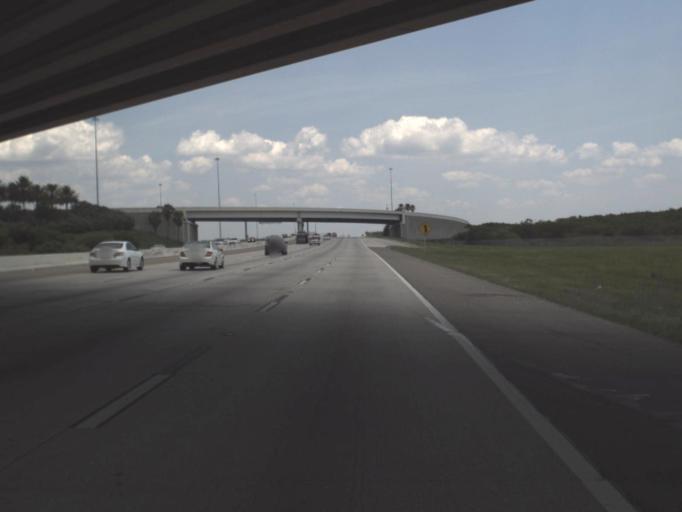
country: US
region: Florida
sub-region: Pinellas County
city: Feather Sound
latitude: 27.8911
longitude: -82.6472
